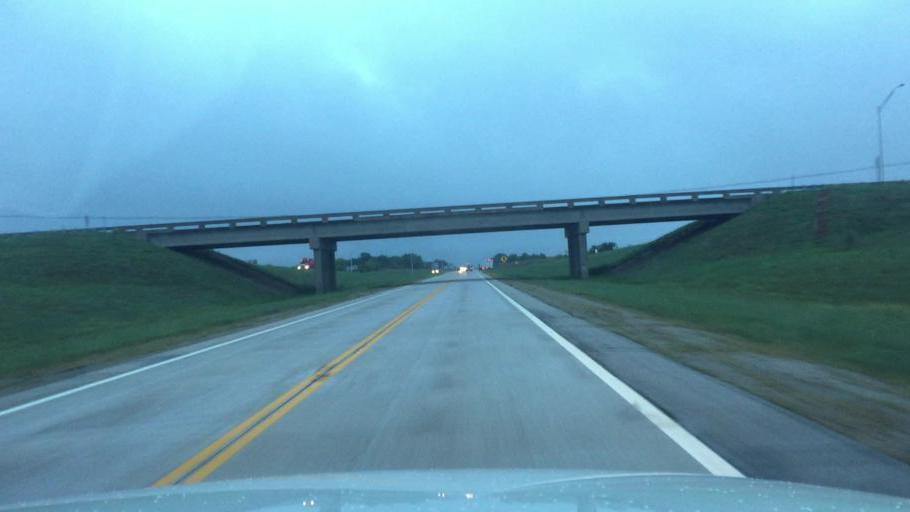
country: US
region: Kansas
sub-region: Neosho County
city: Chanute
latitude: 37.6465
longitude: -95.4797
